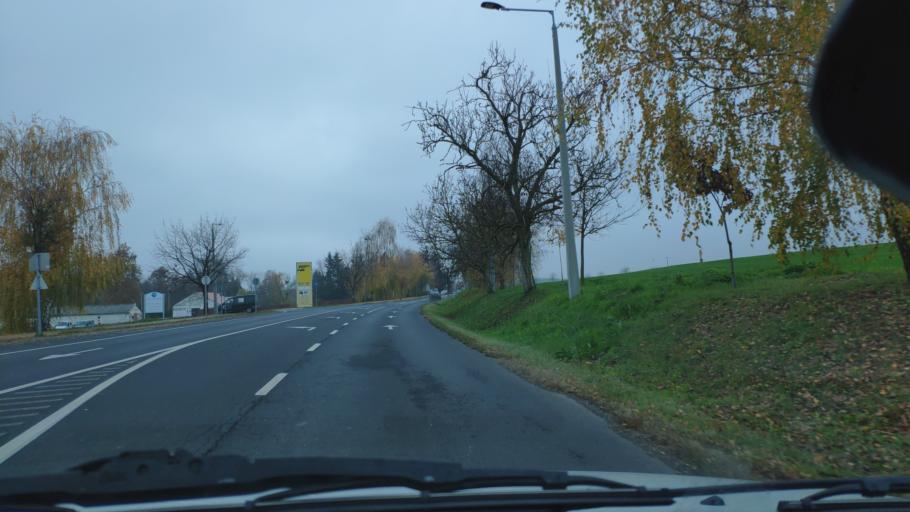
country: HU
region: Zala
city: Zalakomar
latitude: 46.5422
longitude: 17.1261
